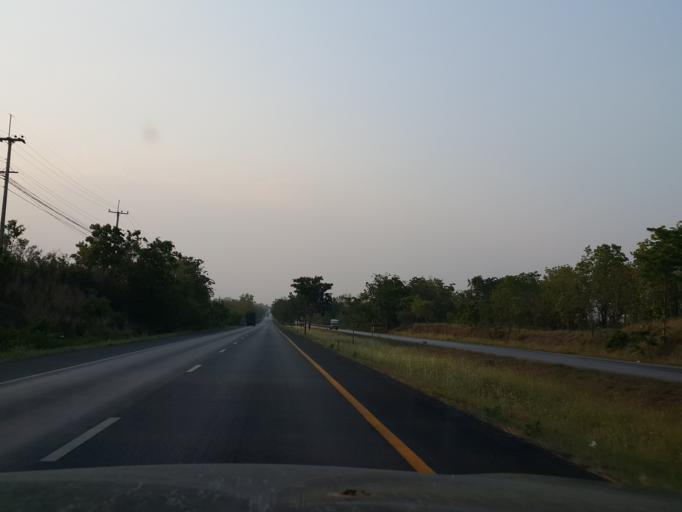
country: TH
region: Lampang
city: Ko Kha
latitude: 18.1089
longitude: 99.3967
